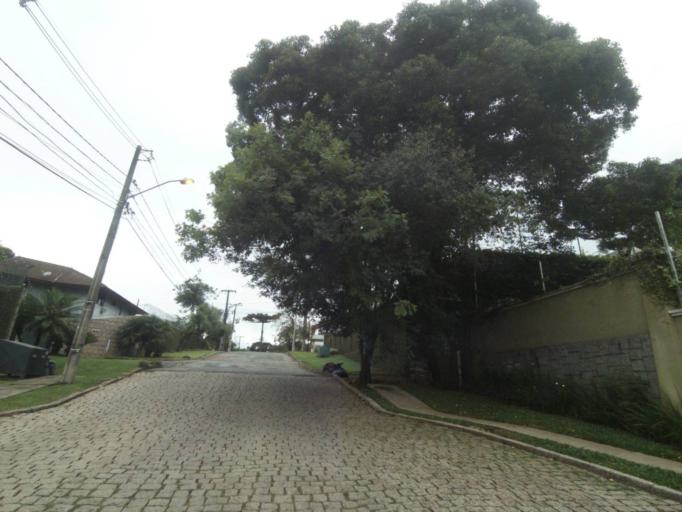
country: BR
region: Parana
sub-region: Curitiba
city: Curitiba
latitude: -25.4520
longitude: -49.3307
